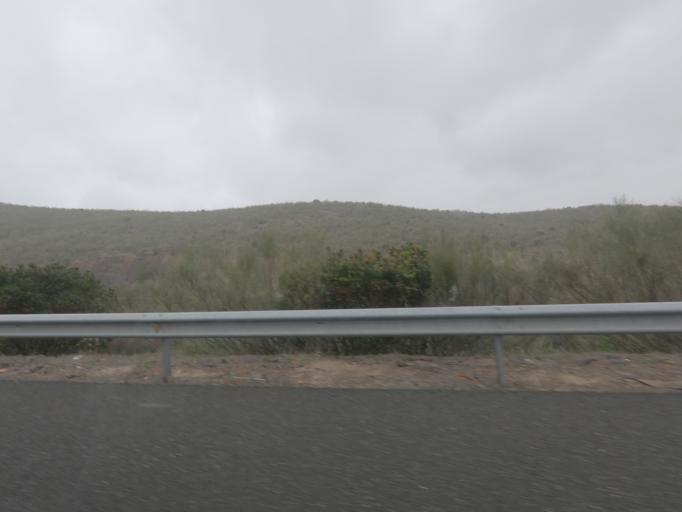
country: ES
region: Extremadura
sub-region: Provincia de Caceres
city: Casas de Millan
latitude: 39.8586
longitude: -6.3148
